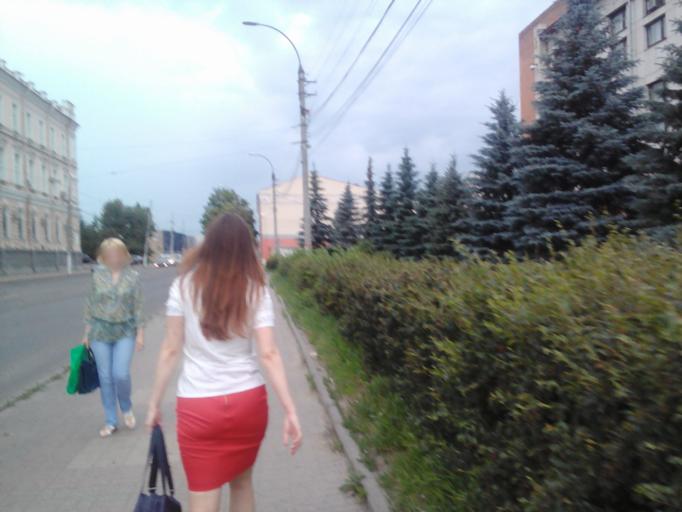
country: RU
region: Kursk
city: Kursk
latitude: 51.7254
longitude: 36.1862
